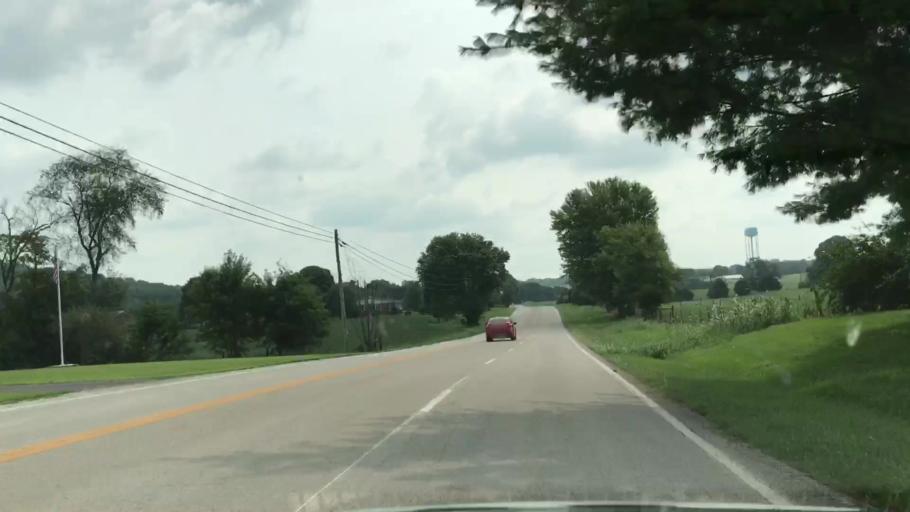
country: US
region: Kentucky
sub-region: Barren County
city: Cave City
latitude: 37.0921
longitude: -86.0871
